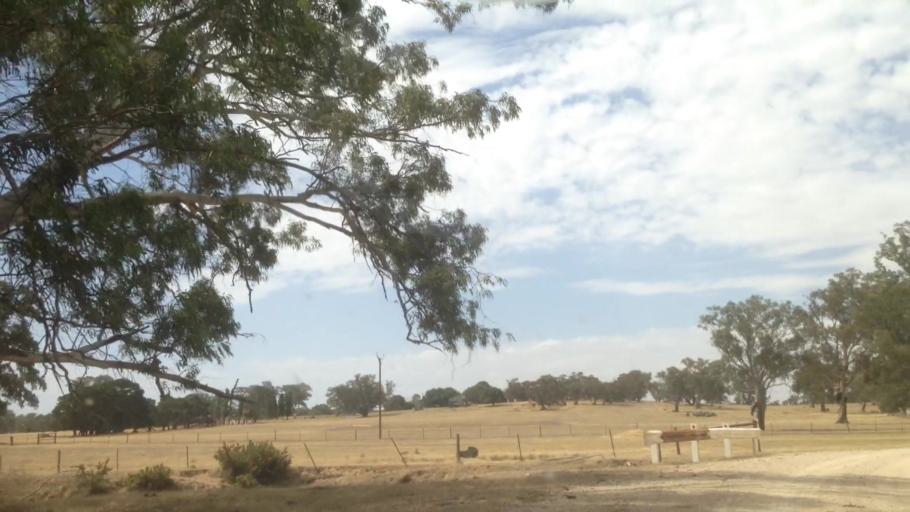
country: AU
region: South Australia
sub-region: Barossa
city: Williamstown
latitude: -34.7020
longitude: 138.9881
